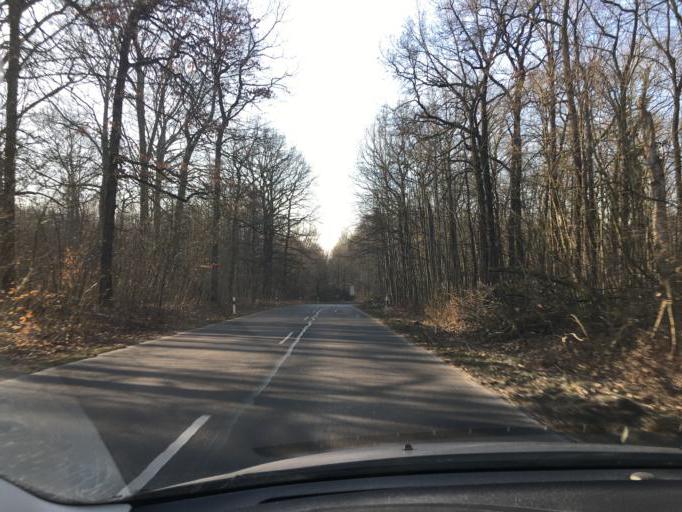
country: DE
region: Thuringia
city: Nobitz
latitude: 50.9821
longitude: 12.5231
